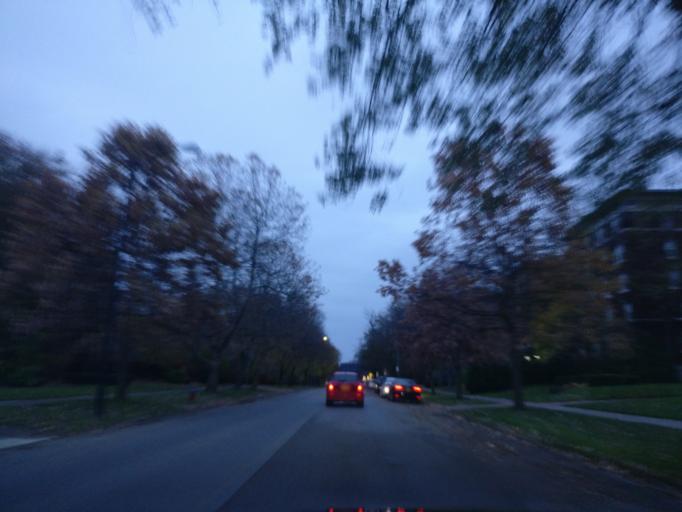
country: US
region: New York
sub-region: Erie County
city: Buffalo
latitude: 42.9154
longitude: -78.8755
